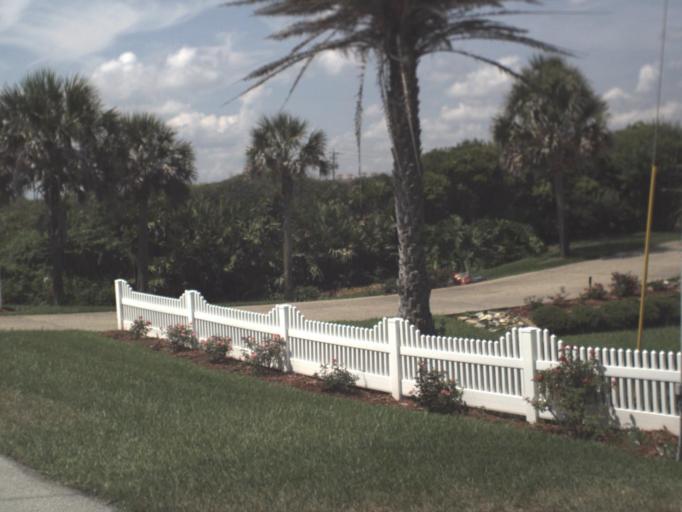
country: US
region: Florida
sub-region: Saint Johns County
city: Villano Beach
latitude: 29.9729
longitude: -81.3107
